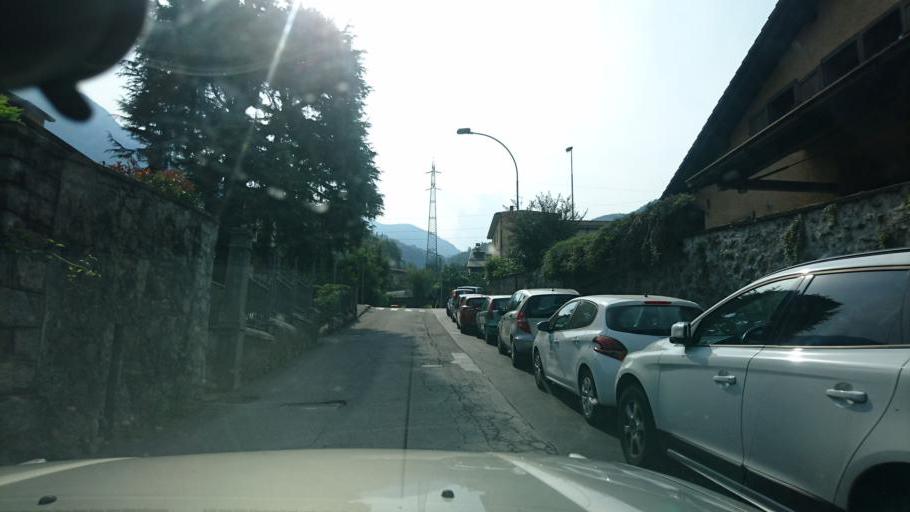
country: IT
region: Lombardy
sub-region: Provincia di Brescia
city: Breno
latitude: 45.9555
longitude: 10.3041
